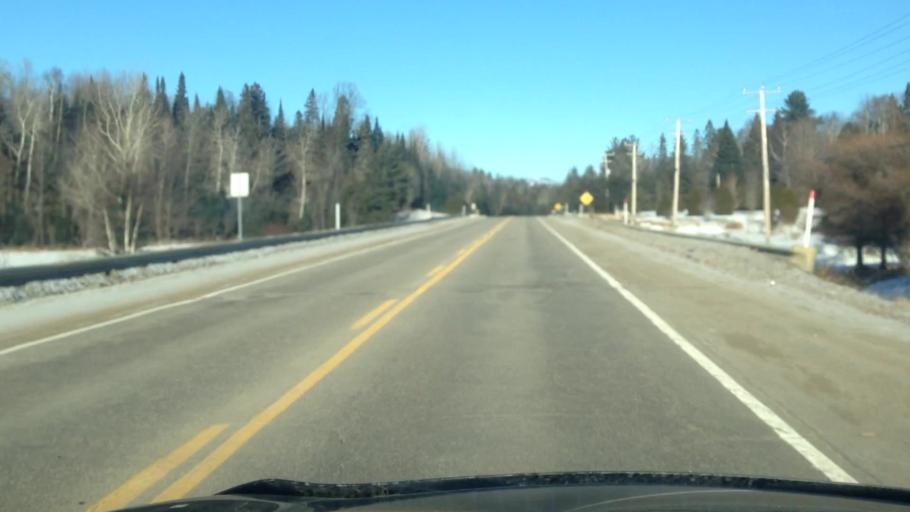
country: CA
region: Quebec
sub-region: Laurentides
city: Mont-Tremblant
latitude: 46.0836
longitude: -74.6121
